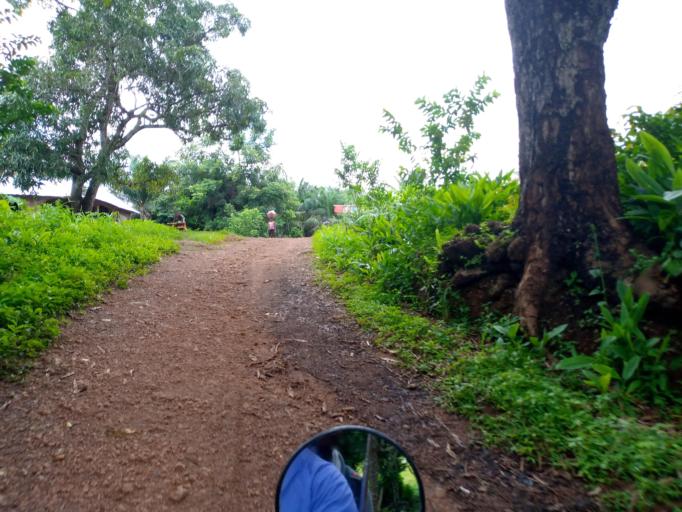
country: SL
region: Northern Province
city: Mange
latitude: 8.9730
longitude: -12.8315
